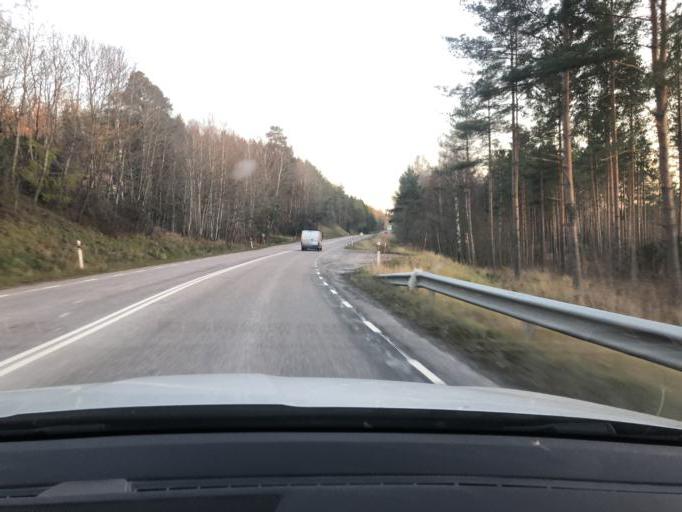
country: SE
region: Soedermanland
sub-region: Strangnas Kommun
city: Akers Styckebruk
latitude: 59.3075
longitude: 17.0918
